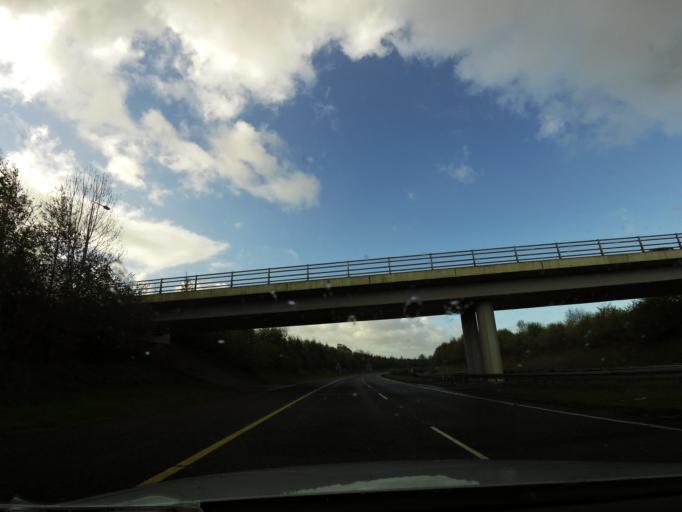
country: IE
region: Munster
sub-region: County Limerick
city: Annacotty
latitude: 52.6667
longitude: -8.5159
